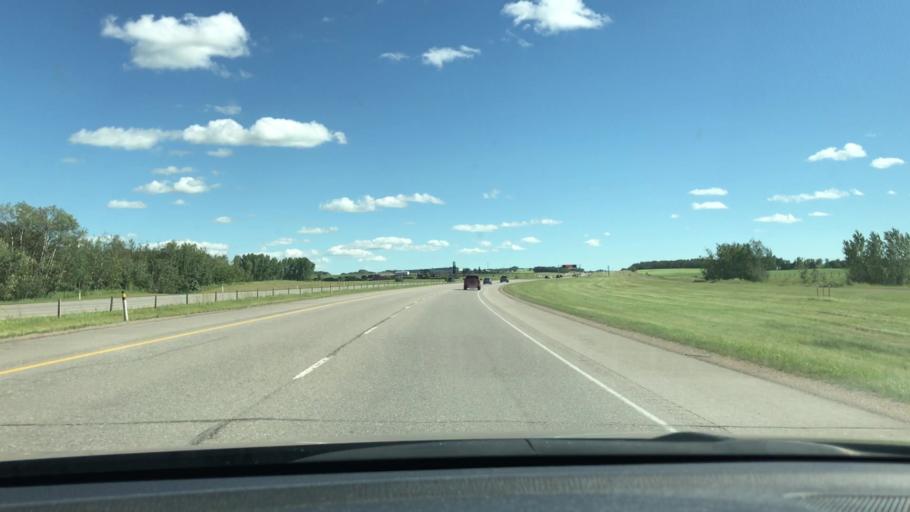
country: CA
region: Alberta
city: Penhold
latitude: 52.1801
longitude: -113.8146
